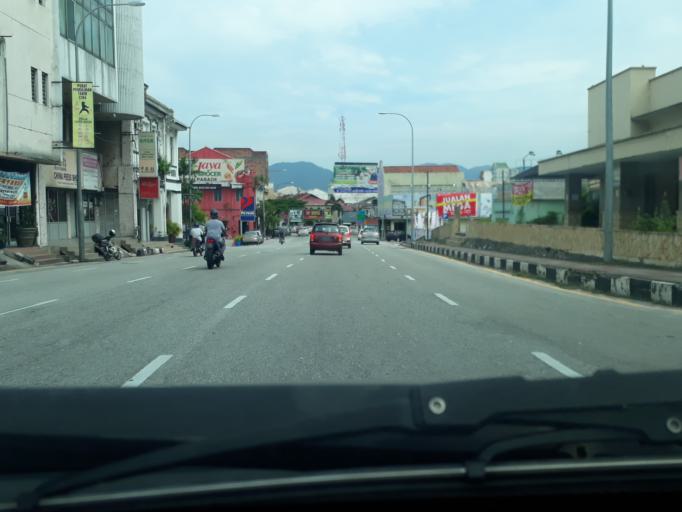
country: MY
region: Perak
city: Ipoh
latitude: 4.5923
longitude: 101.0863
